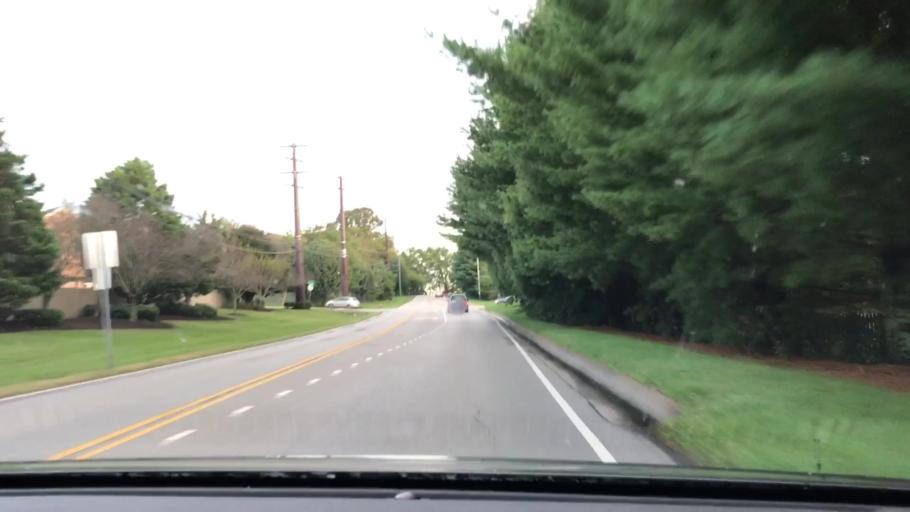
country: US
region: Tennessee
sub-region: Williamson County
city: Brentwood Estates
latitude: 36.0189
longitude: -86.7418
